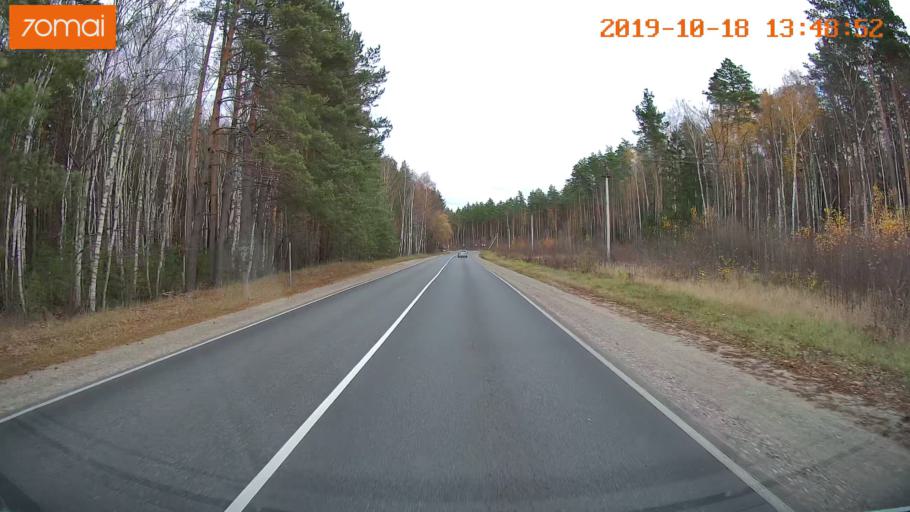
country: RU
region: Moskovskaya
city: Radovitskiy
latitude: 54.9909
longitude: 39.9635
